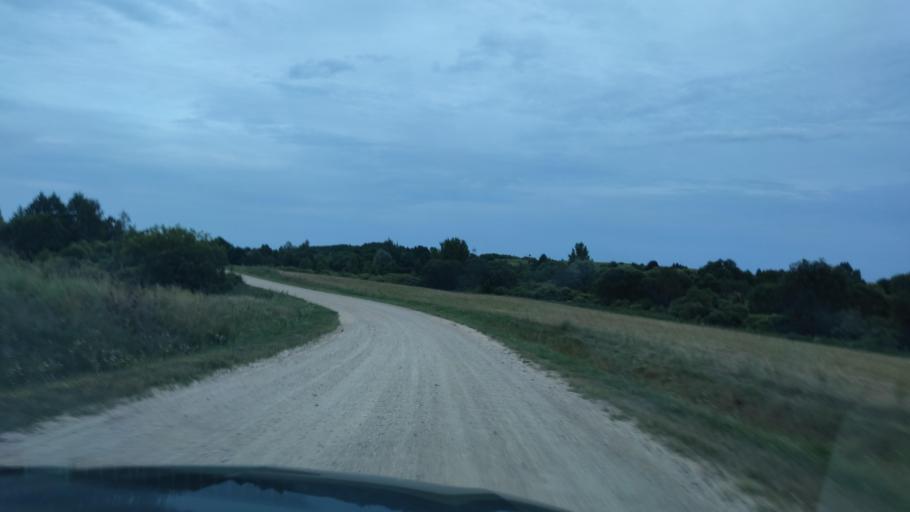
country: BY
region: Vitebsk
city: Mosar
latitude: 55.0740
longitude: 27.2026
